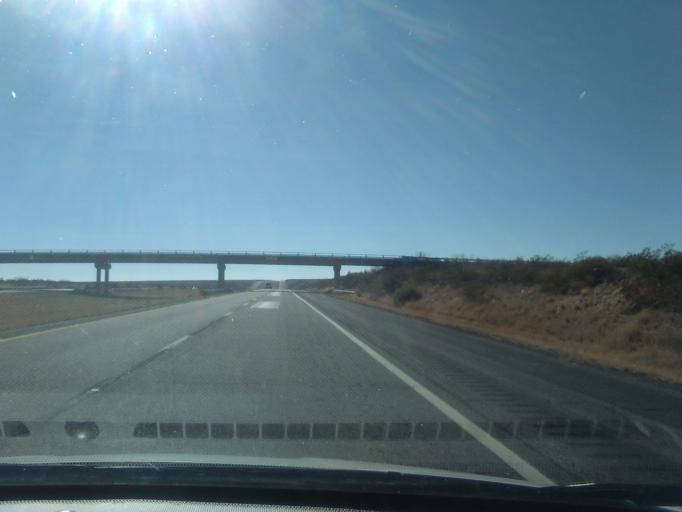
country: US
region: New Mexico
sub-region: Sierra County
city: Elephant Butte
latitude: 33.5964
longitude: -107.1583
